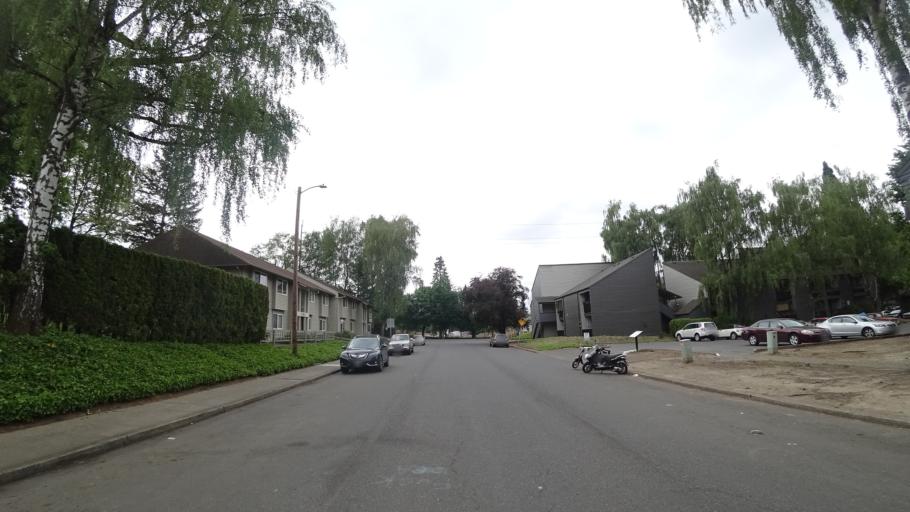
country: US
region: Oregon
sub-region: Clackamas County
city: Milwaukie
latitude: 45.4854
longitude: -122.6343
